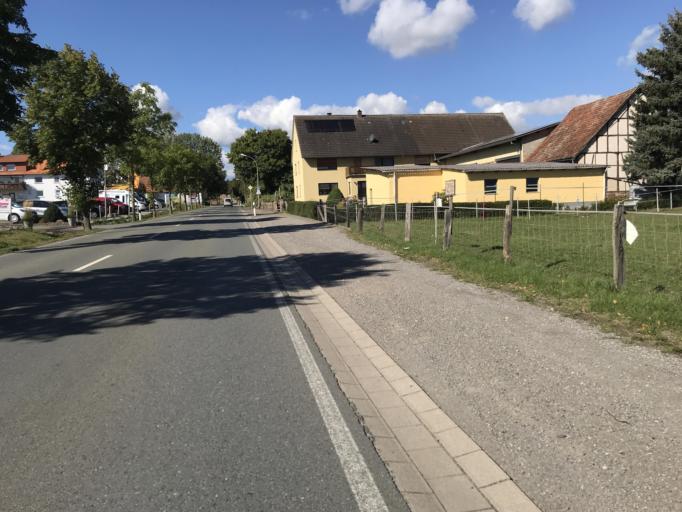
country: DE
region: Hesse
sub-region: Regierungsbezirk Kassel
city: Vohl
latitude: 51.2564
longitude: 8.9327
